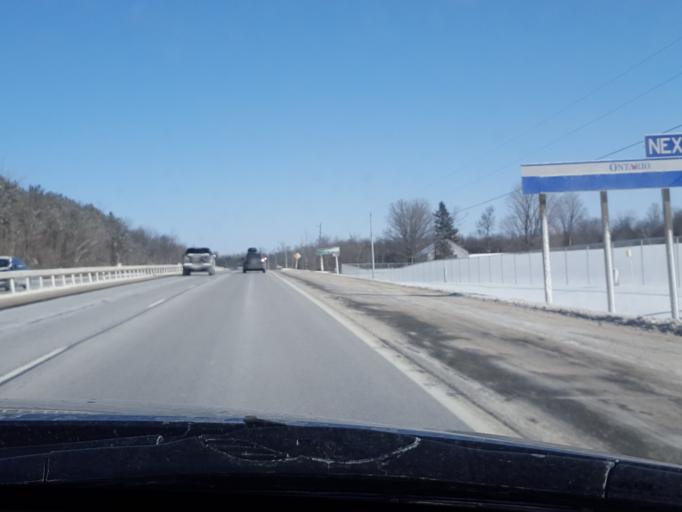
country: CA
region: Ontario
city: Orillia
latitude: 44.4829
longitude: -79.5236
